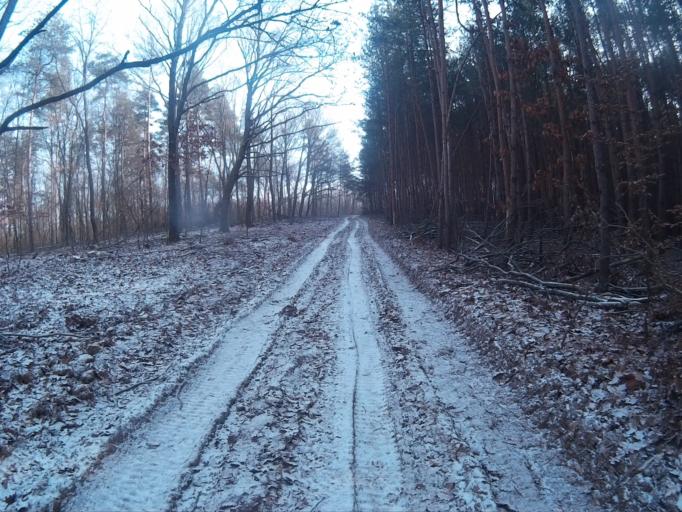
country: HU
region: Borsod-Abauj-Zemplen
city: Szendro
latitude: 48.4931
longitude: 20.7937
